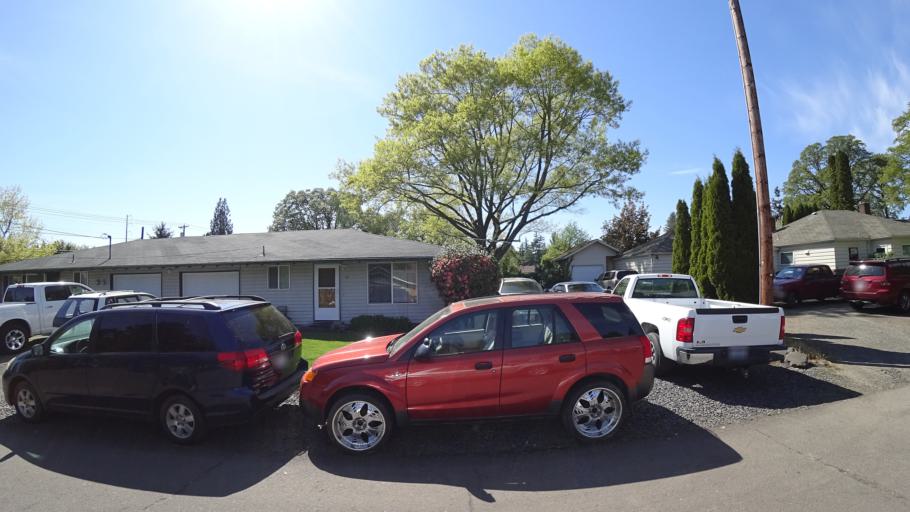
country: US
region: Oregon
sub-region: Washington County
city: Hillsboro
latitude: 45.5222
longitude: -122.9702
